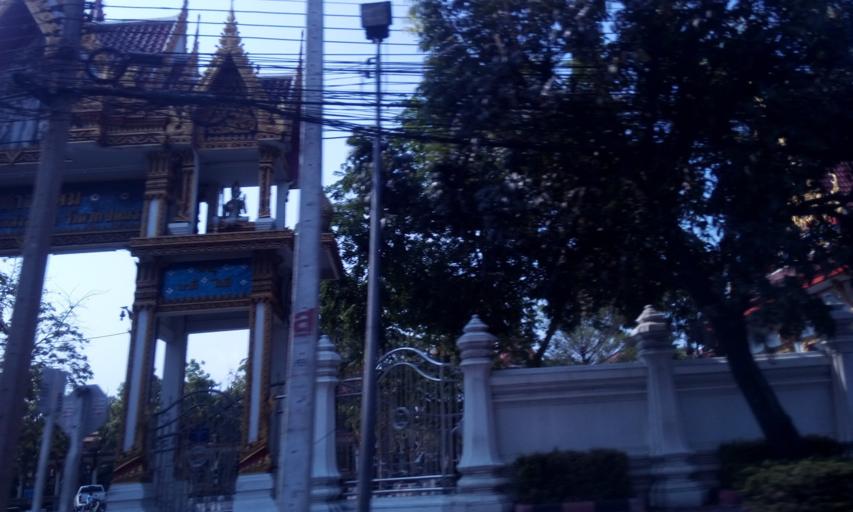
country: TH
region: Bangkok
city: Sai Mai
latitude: 13.9320
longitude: 100.6582
